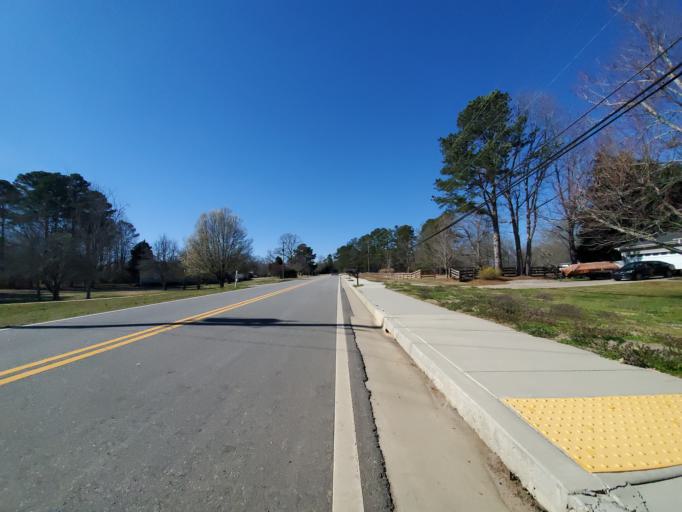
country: US
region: Georgia
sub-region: Gwinnett County
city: Dacula
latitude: 33.9803
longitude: -83.8790
